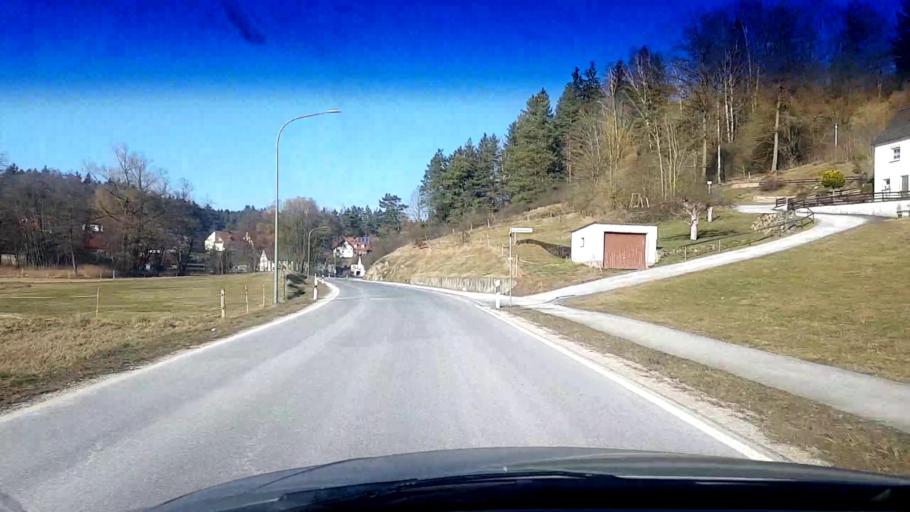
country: DE
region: Bavaria
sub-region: Upper Franconia
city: Aufsess
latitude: 49.9076
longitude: 11.2233
